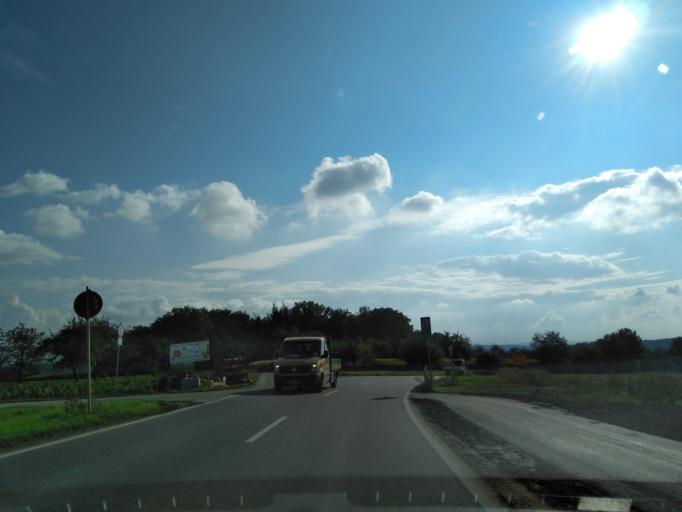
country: DE
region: Baden-Wuerttemberg
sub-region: Regierungsbezirk Stuttgart
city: Oberriexingen
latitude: 48.9475
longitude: 9.0548
